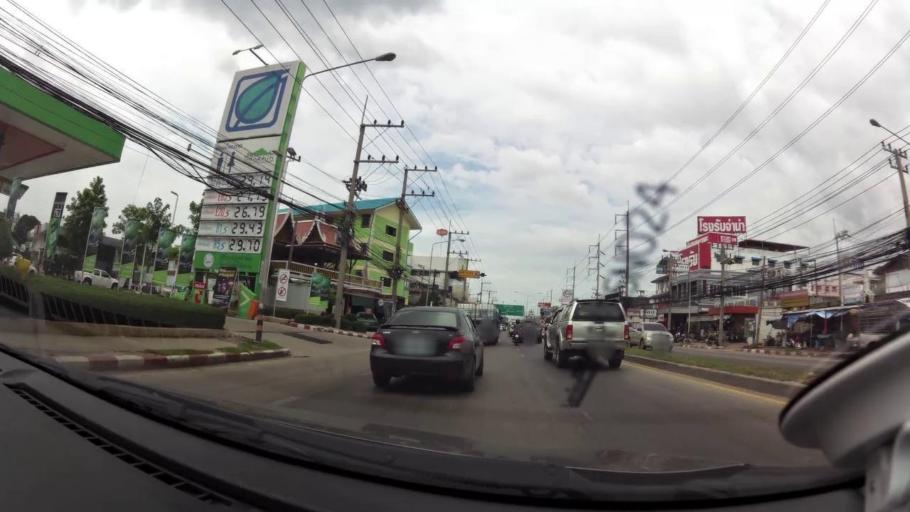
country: TH
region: Samut Sakhon
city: Samut Sakhon
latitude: 13.5675
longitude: 100.2720
